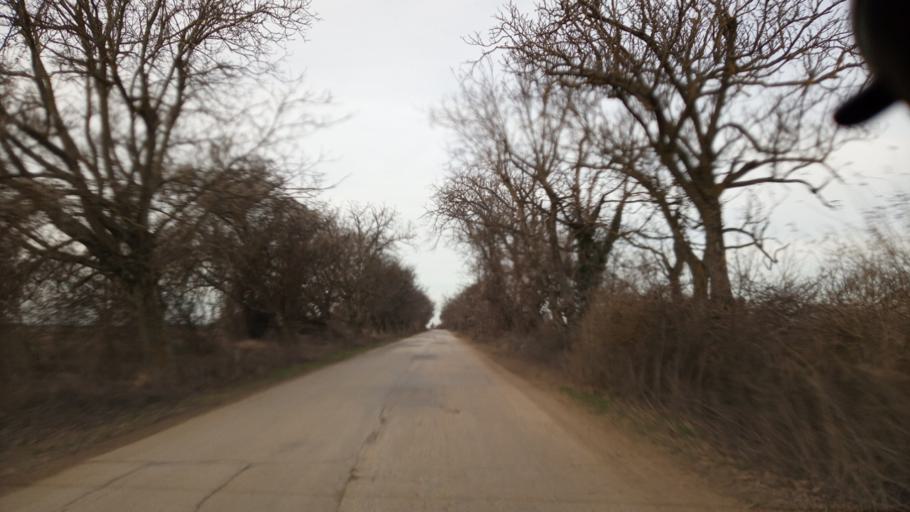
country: BG
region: Pleven
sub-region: Obshtina Nikopol
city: Nikopol
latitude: 43.5963
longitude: 24.9702
